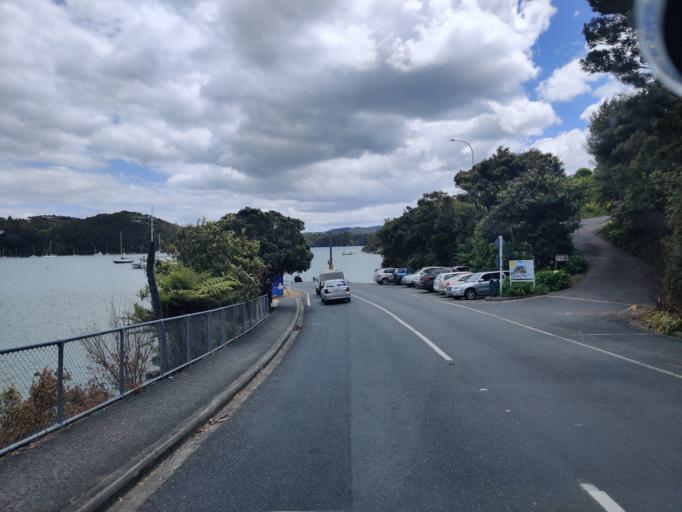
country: NZ
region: Northland
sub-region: Far North District
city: Paihia
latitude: -35.3052
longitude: 174.1196
